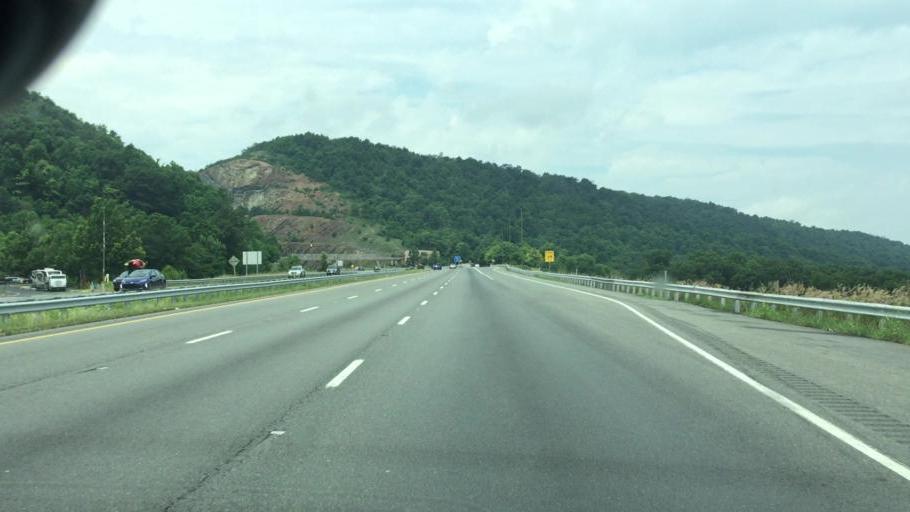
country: US
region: Maryland
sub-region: Washington County
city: Hancock
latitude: 39.7142
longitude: -78.2792
